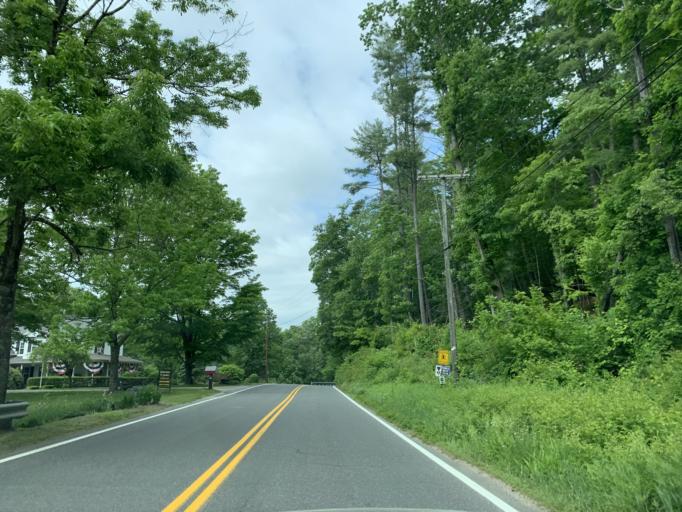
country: US
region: Massachusetts
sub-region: Hampshire County
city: Westhampton
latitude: 42.2445
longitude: -72.8623
